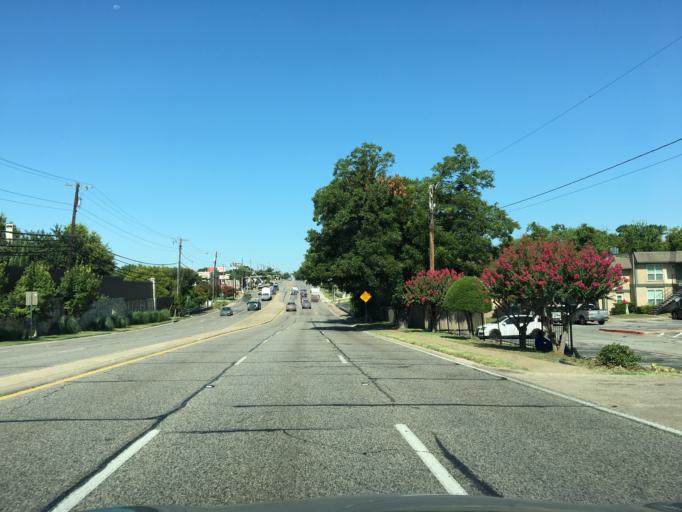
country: US
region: Texas
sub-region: Dallas County
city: Garland
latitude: 32.8643
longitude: -96.6979
